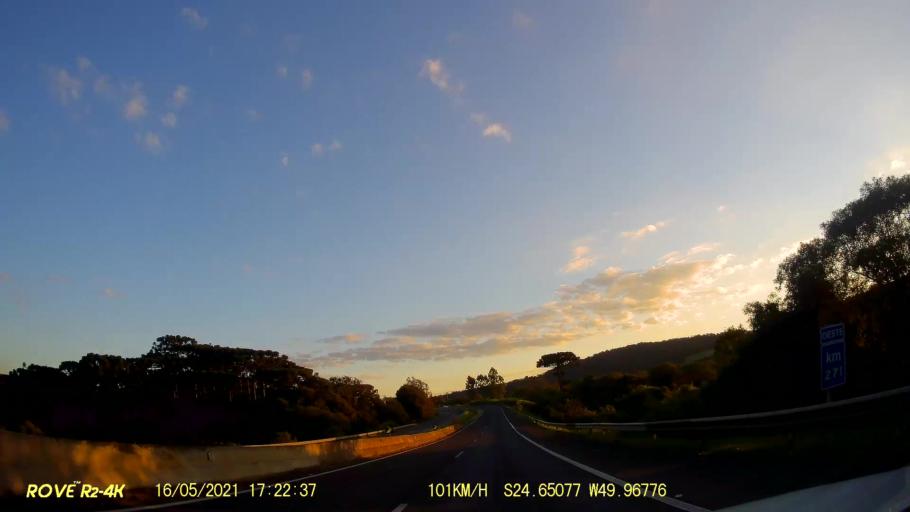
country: BR
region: Parana
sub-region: Pirai Do Sul
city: Pirai do Sul
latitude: -24.6511
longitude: -49.9680
